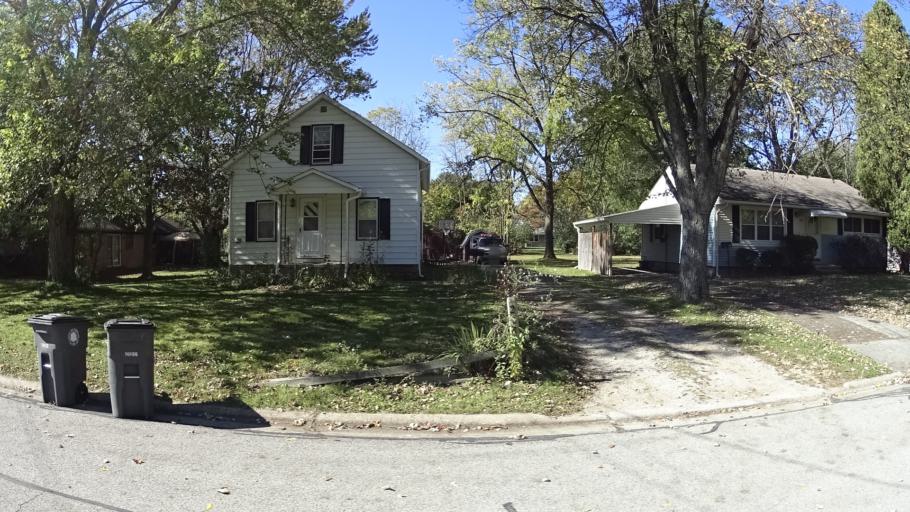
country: US
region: Ohio
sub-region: Lorain County
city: Oberlin
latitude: 41.2987
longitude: -82.2264
